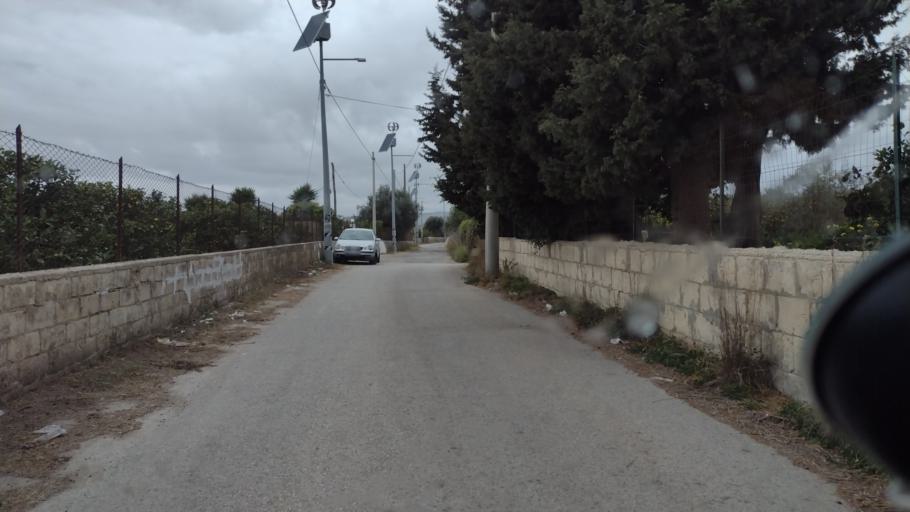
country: IT
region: Sicily
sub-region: Provincia di Siracusa
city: Avola
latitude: 36.8863
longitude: 15.1229
